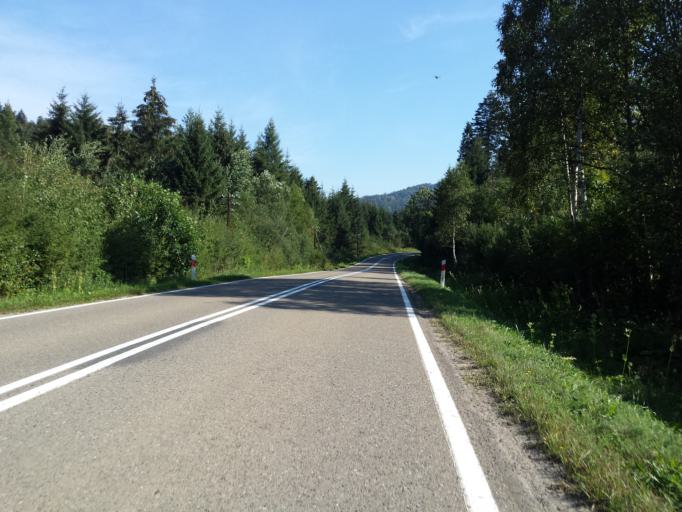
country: PL
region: Subcarpathian Voivodeship
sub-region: Powiat leski
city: Baligrod
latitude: 49.2980
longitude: 22.2717
